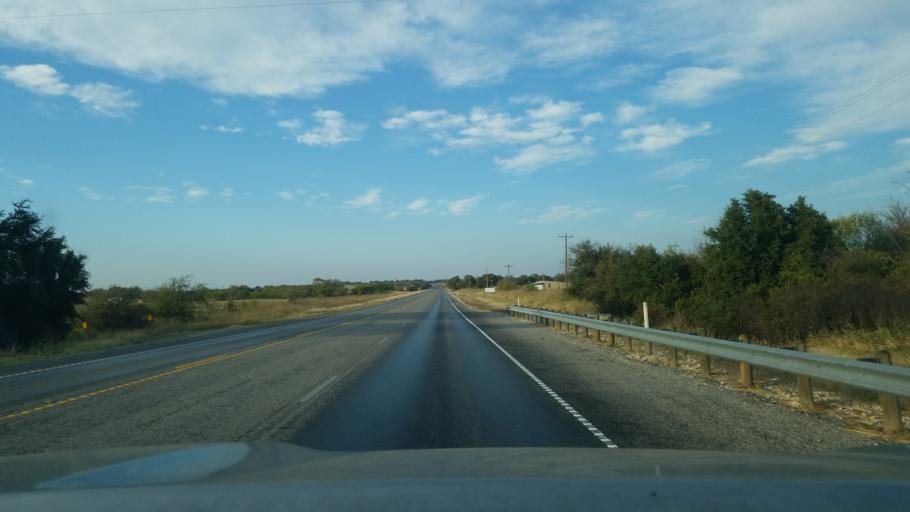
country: US
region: Texas
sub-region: Brown County
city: Lake Brownwood
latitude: 31.9942
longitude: -98.9209
